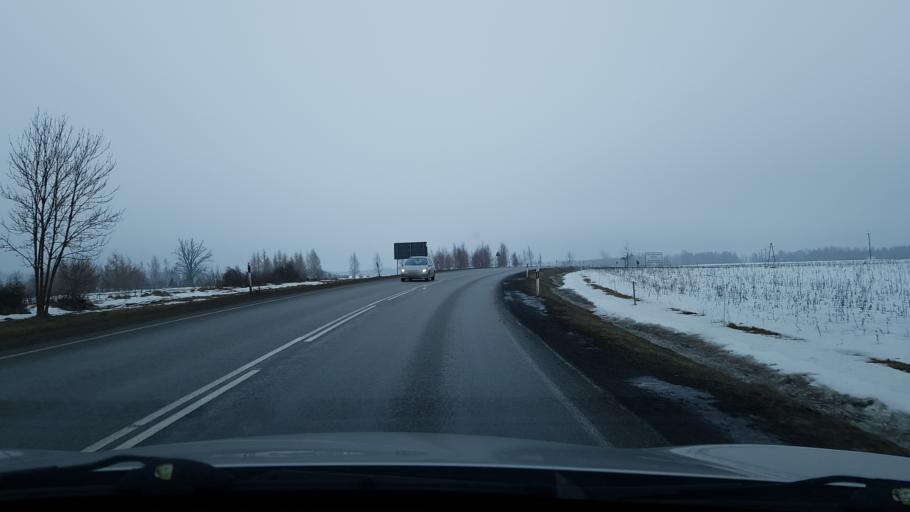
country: EE
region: Valgamaa
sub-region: Valga linn
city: Valga
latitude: 57.9210
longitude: 26.1817
